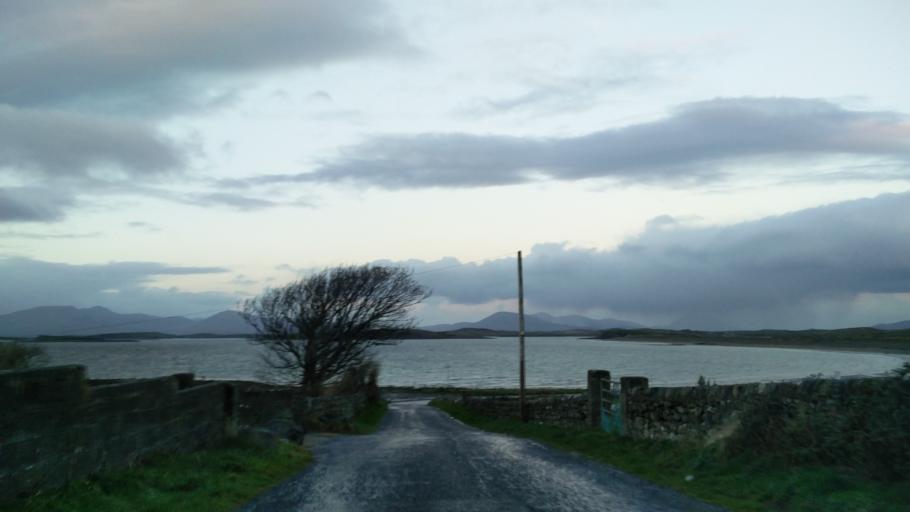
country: IE
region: Connaught
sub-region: Maigh Eo
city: Westport
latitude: 53.7867
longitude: -9.6656
